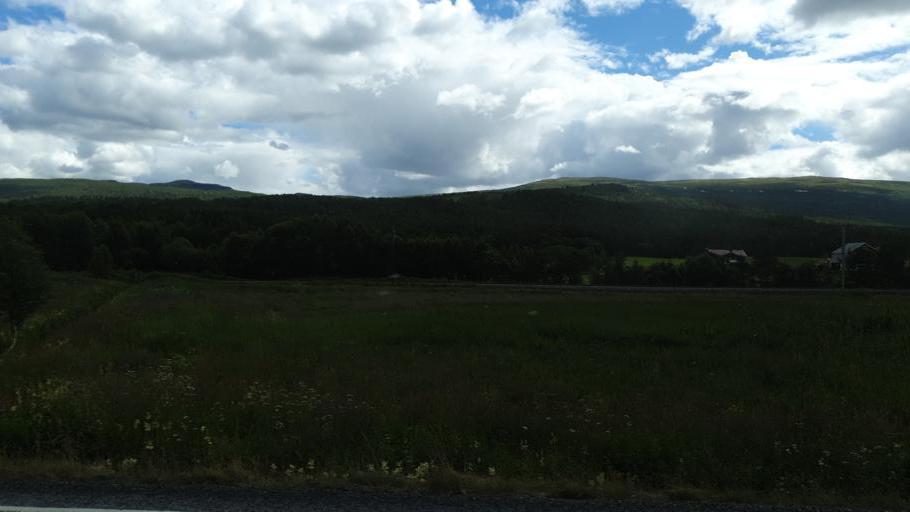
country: NO
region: Sor-Trondelag
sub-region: Oppdal
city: Oppdal
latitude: 62.6262
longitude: 9.7731
